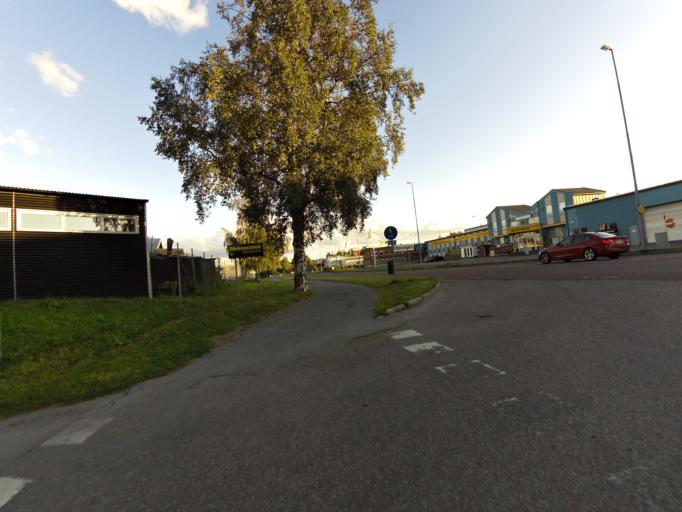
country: SE
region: Gaevleborg
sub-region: Gavle Kommun
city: Gavle
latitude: 60.6846
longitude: 17.1524
